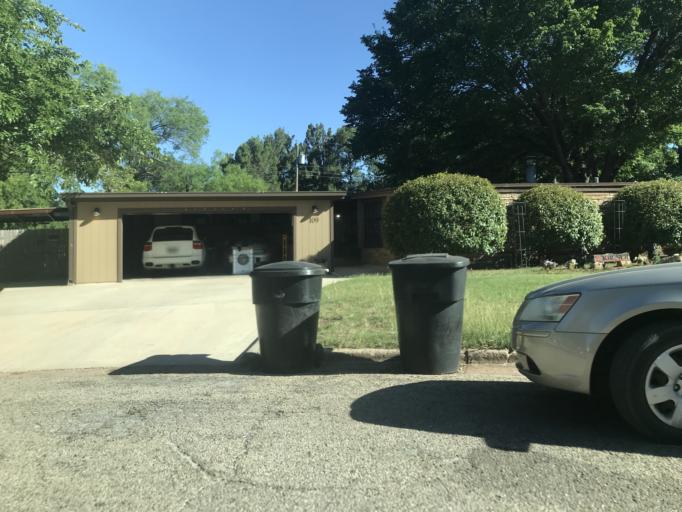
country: US
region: Texas
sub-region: Taylor County
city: Abilene
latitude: 32.4306
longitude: -99.7681
